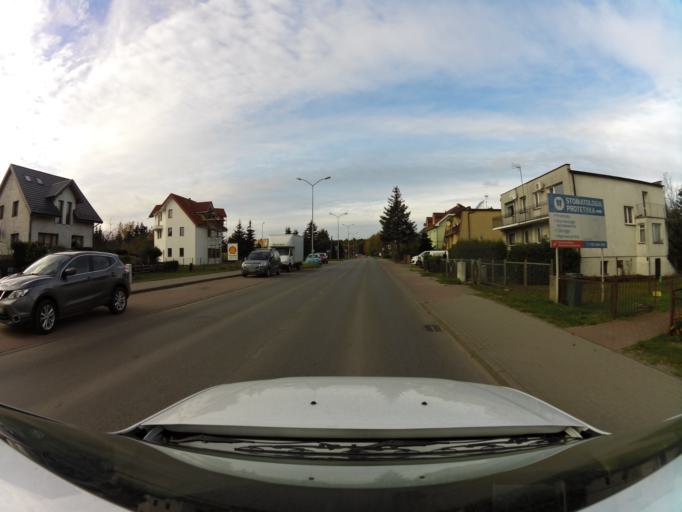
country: PL
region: West Pomeranian Voivodeship
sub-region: Powiat gryficki
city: Gryfice
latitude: 53.9210
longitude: 15.1858
